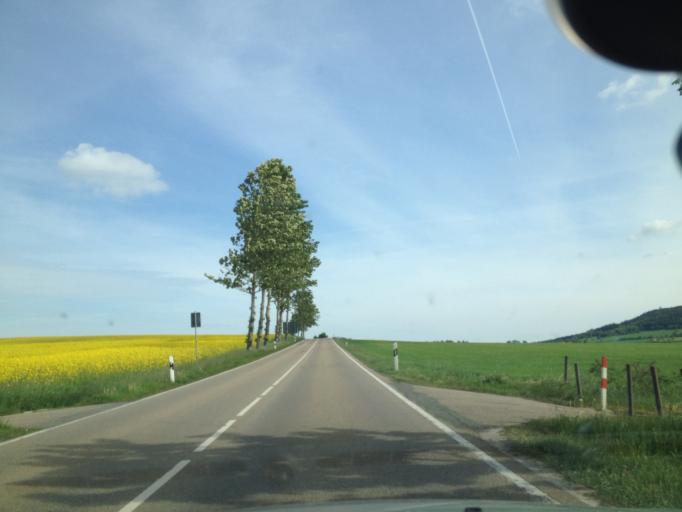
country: DE
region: Saxony
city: Annaberg-Buchholz
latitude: 50.5509
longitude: 13.0177
